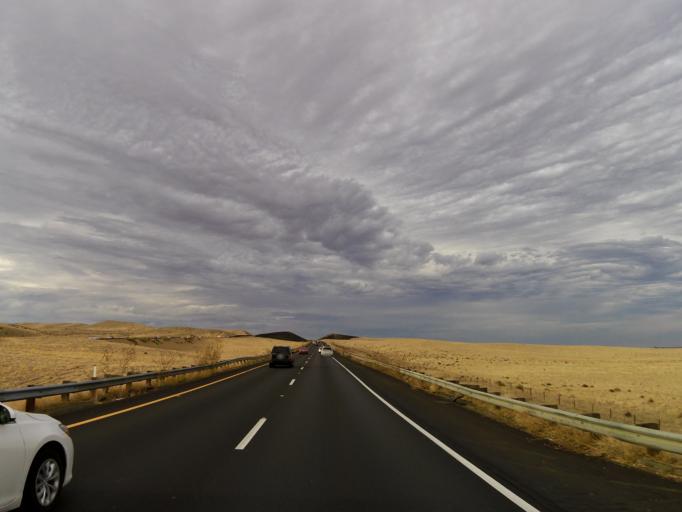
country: US
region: California
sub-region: Fresno County
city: Coalinga
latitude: 36.3148
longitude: -120.2852
